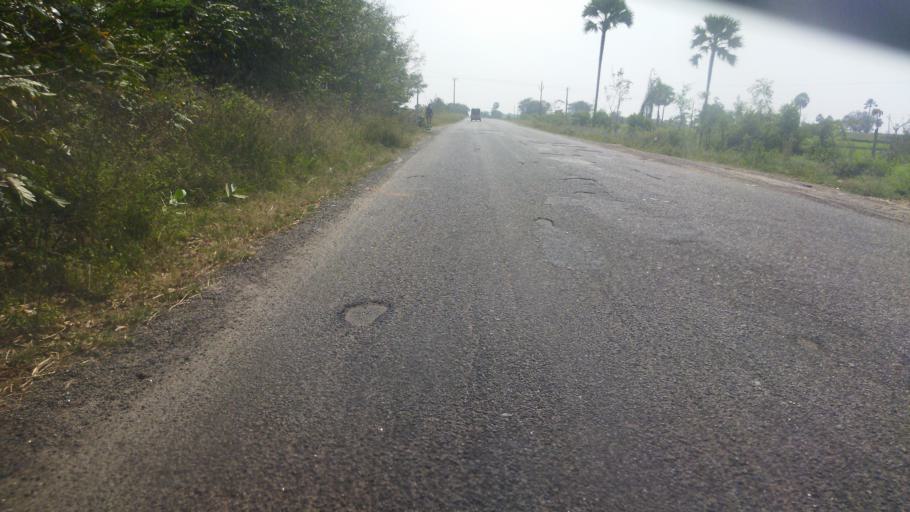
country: IN
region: Telangana
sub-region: Nalgonda
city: Nalgonda
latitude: 17.1024
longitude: 79.2830
